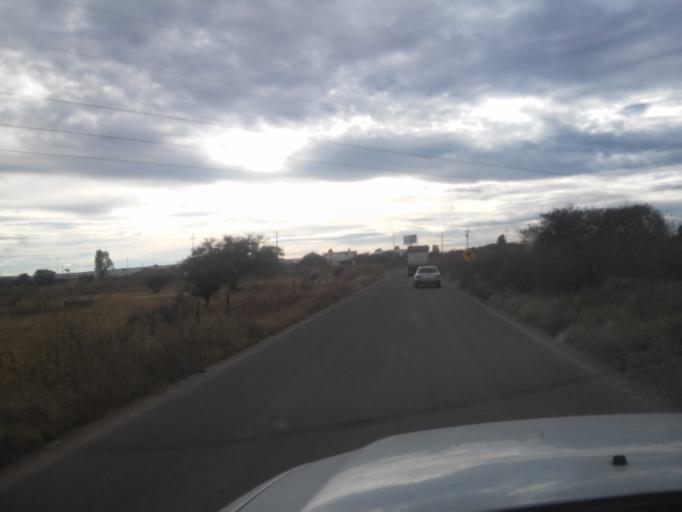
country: MX
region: Durango
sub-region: Durango
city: Jose Refugio Salcido
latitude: 24.0288
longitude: -104.5728
